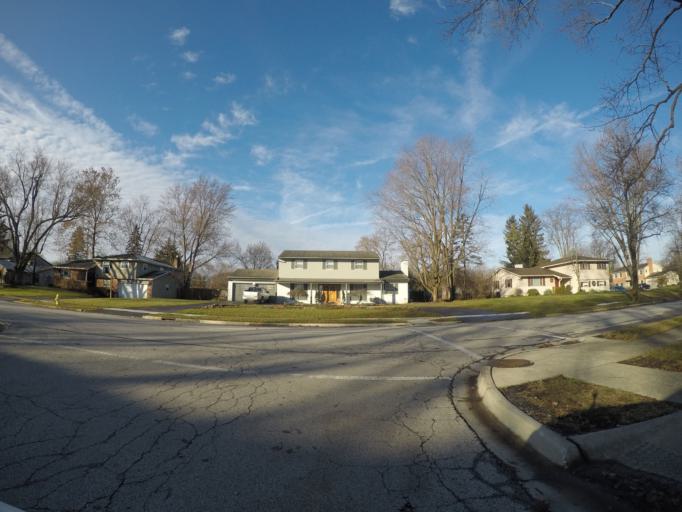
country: US
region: Ohio
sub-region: Franklin County
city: Upper Arlington
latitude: 40.0442
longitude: -83.0810
